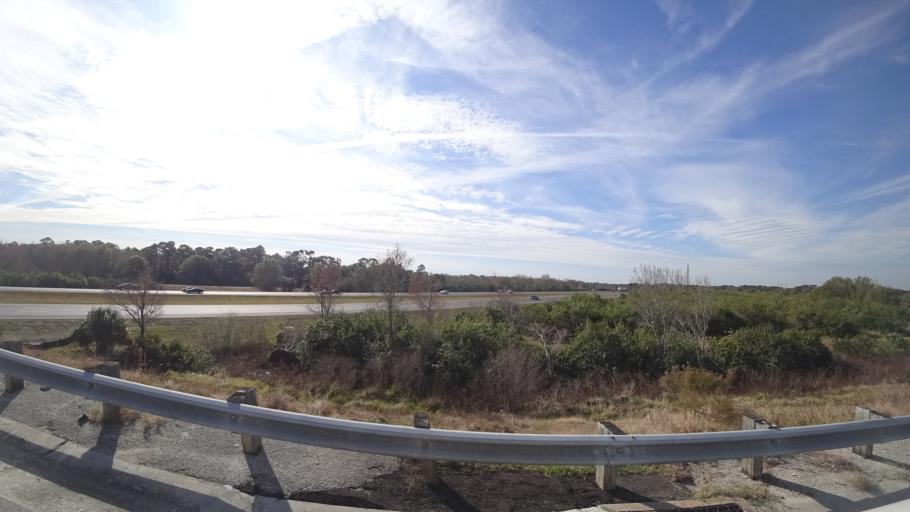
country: US
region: Florida
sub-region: Hillsborough County
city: Ruskin
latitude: 27.6233
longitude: -82.4782
